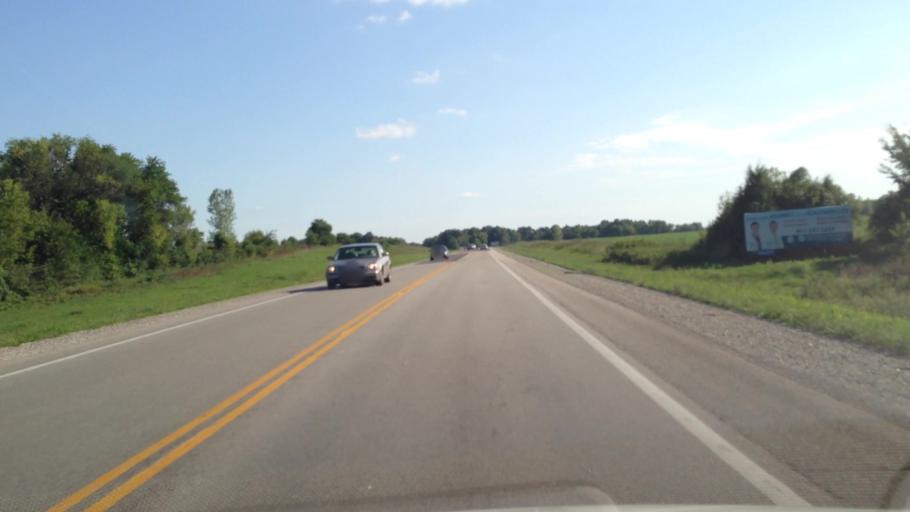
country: US
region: Kansas
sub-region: Crawford County
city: Arma
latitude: 37.5353
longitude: -94.7103
